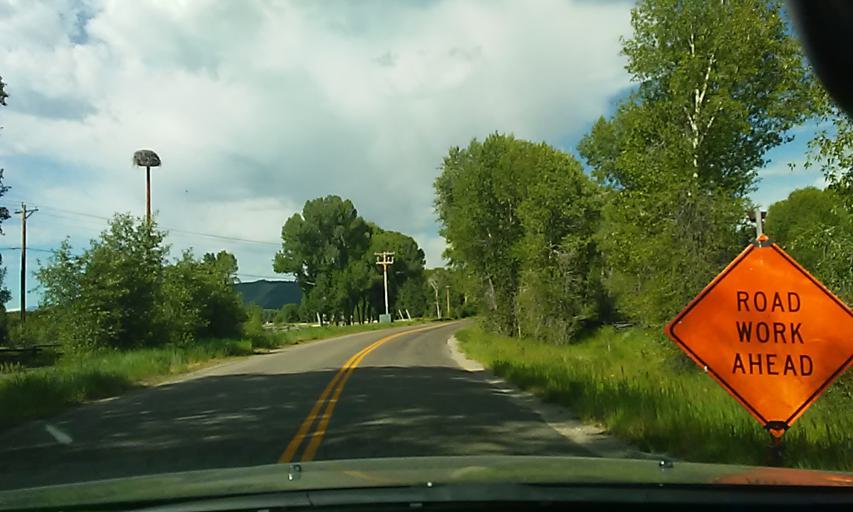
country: US
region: Wyoming
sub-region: Teton County
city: Jackson
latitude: 43.5626
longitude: -110.7543
